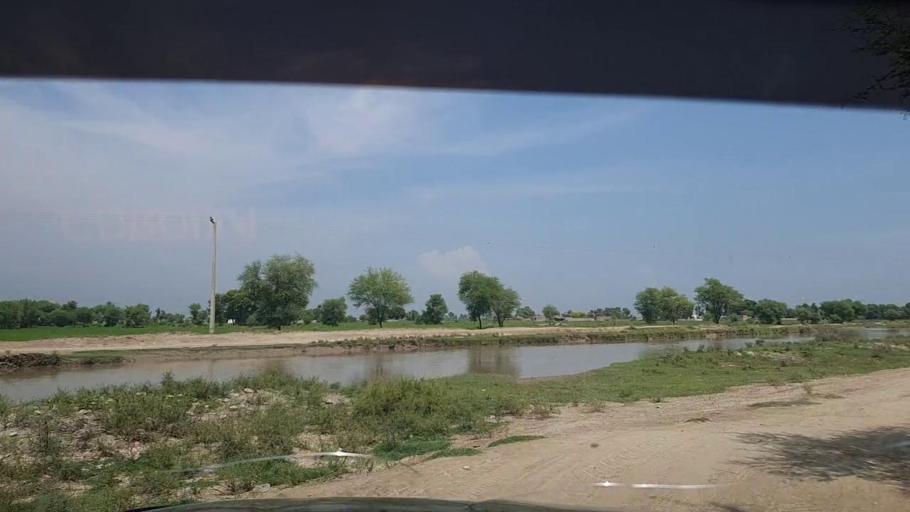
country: PK
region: Sindh
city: Tangwani
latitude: 28.2302
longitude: 68.9314
